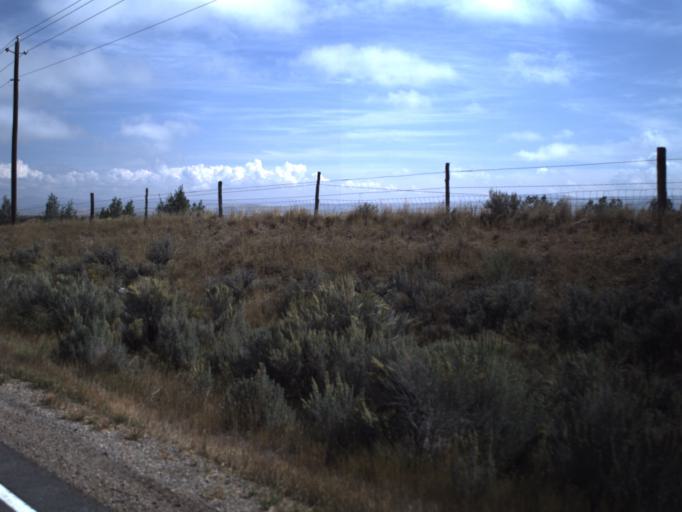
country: US
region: Utah
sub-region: Rich County
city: Randolph
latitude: 41.7680
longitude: -111.1246
